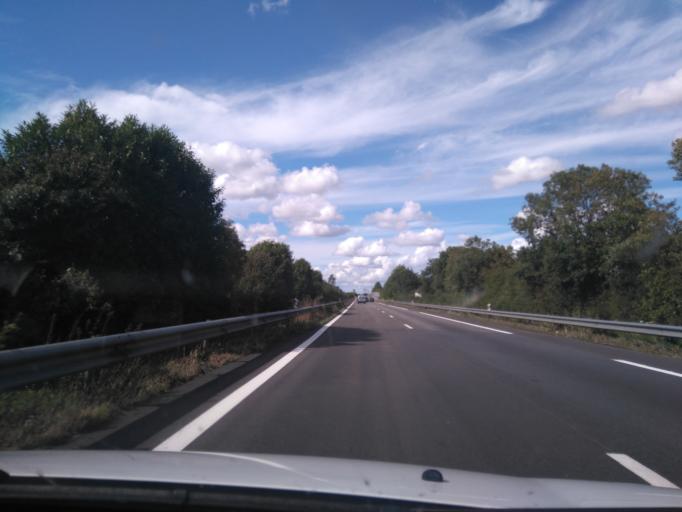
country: FR
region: Pays de la Loire
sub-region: Departement de la Loire-Atlantique
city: Heric
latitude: 47.4308
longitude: -1.6377
